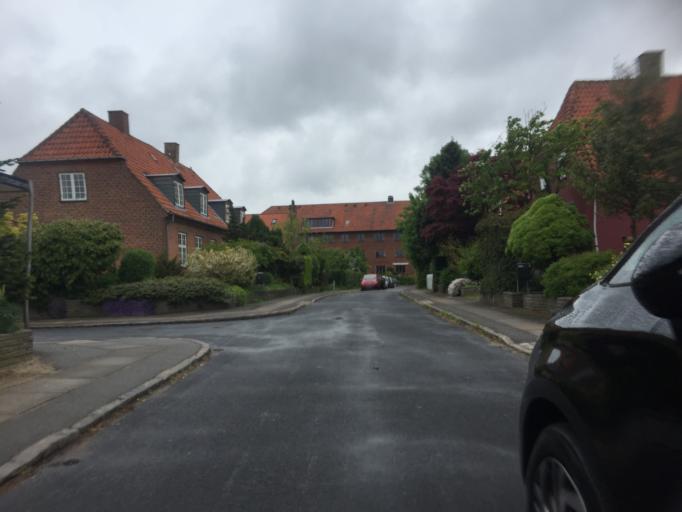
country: DK
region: Capital Region
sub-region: Frederiksberg Kommune
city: Frederiksberg
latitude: 55.6969
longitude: 12.5194
